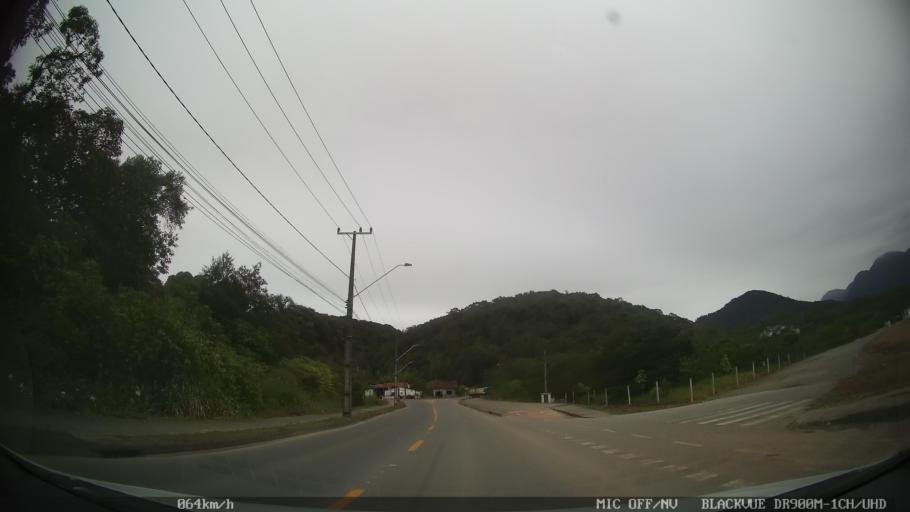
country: BR
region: Santa Catarina
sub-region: Joinville
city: Joinville
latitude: -26.2782
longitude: -48.9225
